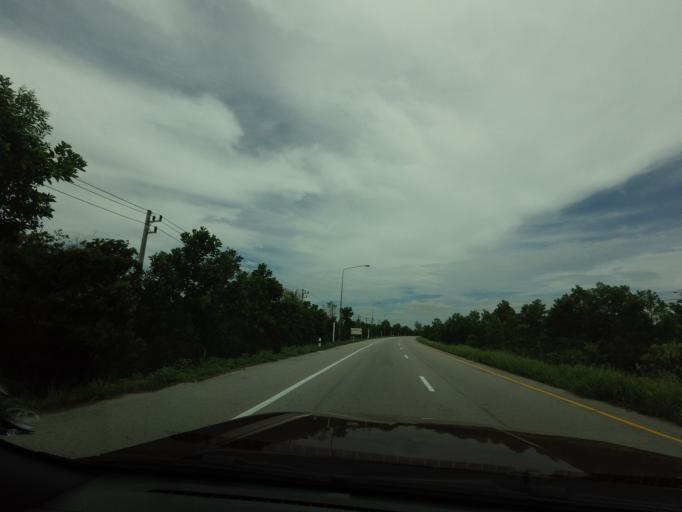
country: TH
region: Narathiwat
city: Narathiwat
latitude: 6.3453
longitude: 101.8771
